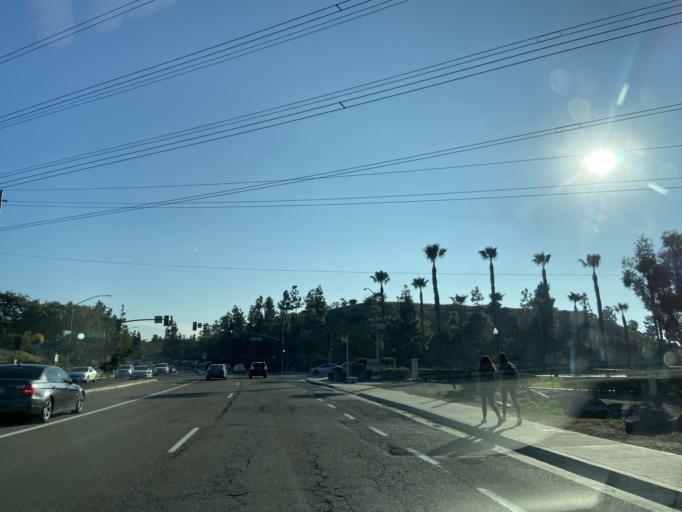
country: US
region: California
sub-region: San Diego County
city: Bonita
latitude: 32.6367
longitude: -116.9673
